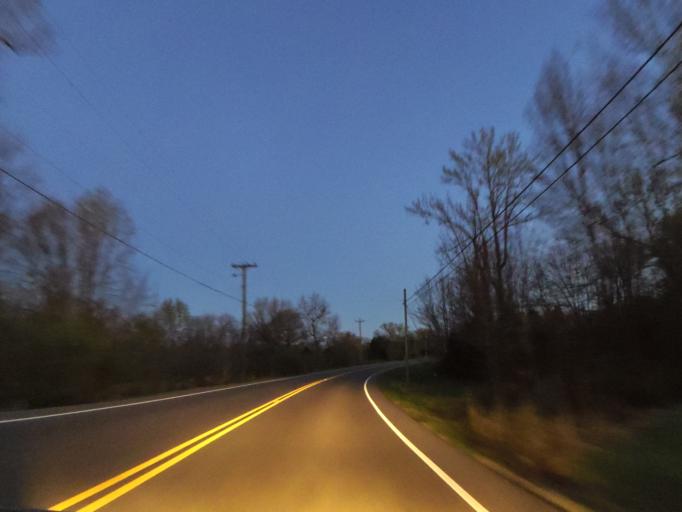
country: US
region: Tennessee
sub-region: Robertson County
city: Greenbrier
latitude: 36.3573
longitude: -86.8822
